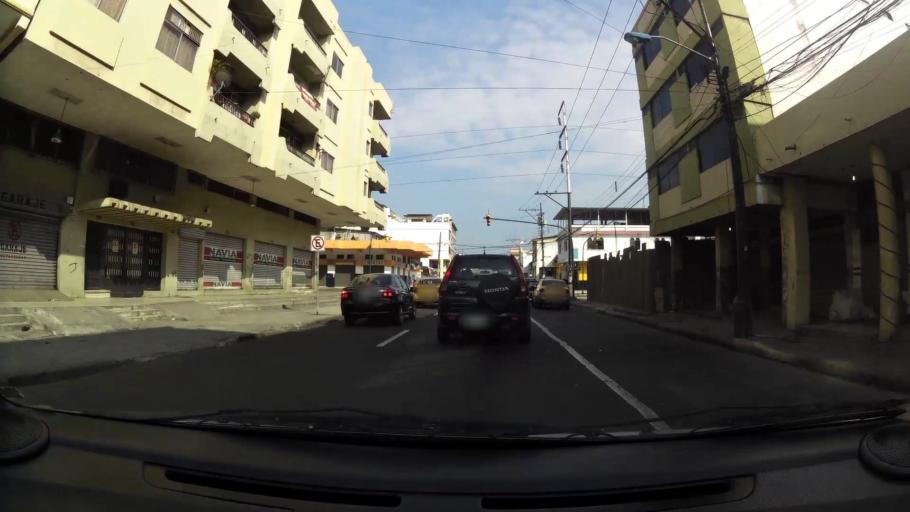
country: EC
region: Guayas
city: Guayaquil
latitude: -2.1943
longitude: -79.8942
